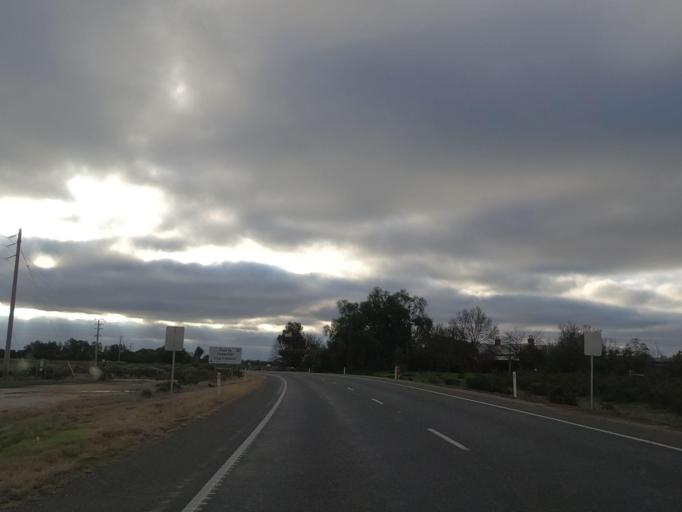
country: AU
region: Victoria
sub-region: Swan Hill
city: Swan Hill
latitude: -35.7245
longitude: 143.8899
